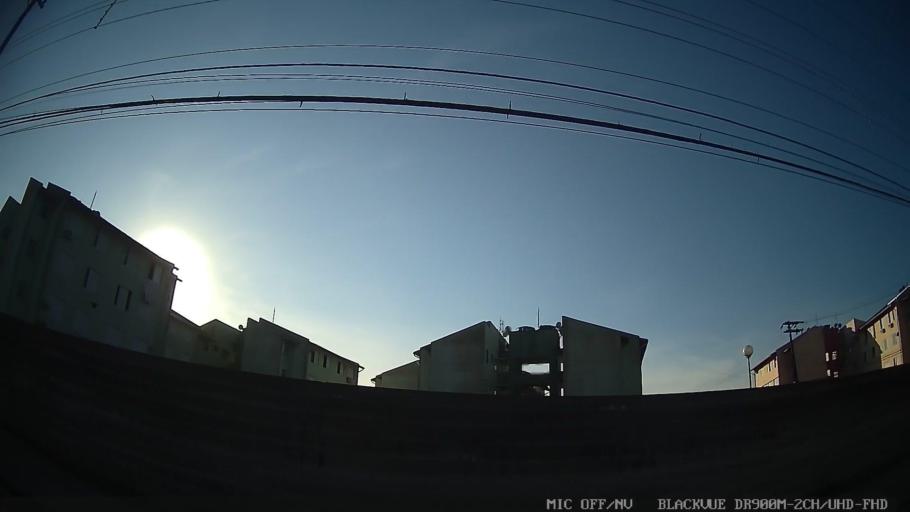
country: BR
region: Sao Paulo
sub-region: Guaruja
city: Guaruja
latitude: -23.9636
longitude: -46.2477
